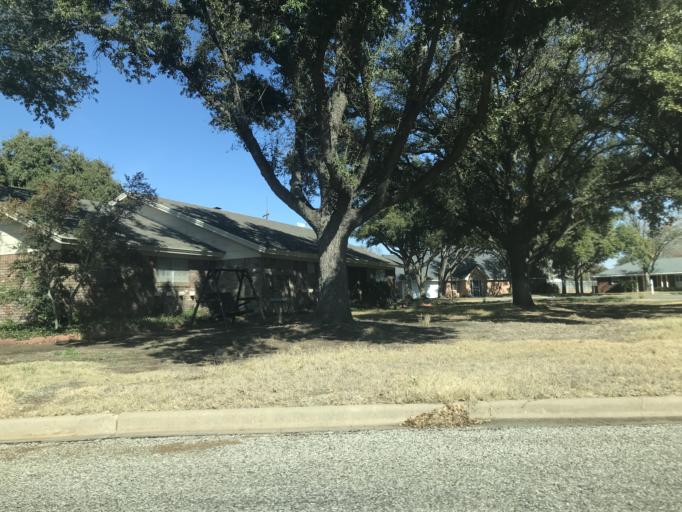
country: US
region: Texas
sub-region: Tom Green County
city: San Angelo
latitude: 31.4272
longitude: -100.4757
